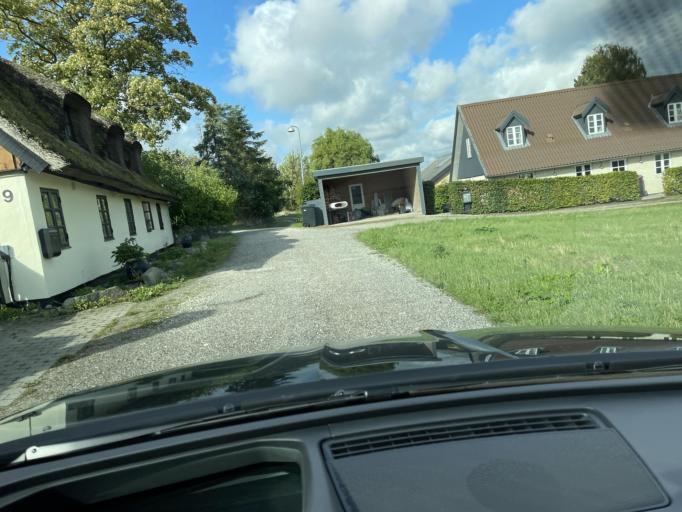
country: DK
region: Zealand
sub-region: Solrod Kommune
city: Havdrup
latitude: 55.5667
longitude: 12.1087
